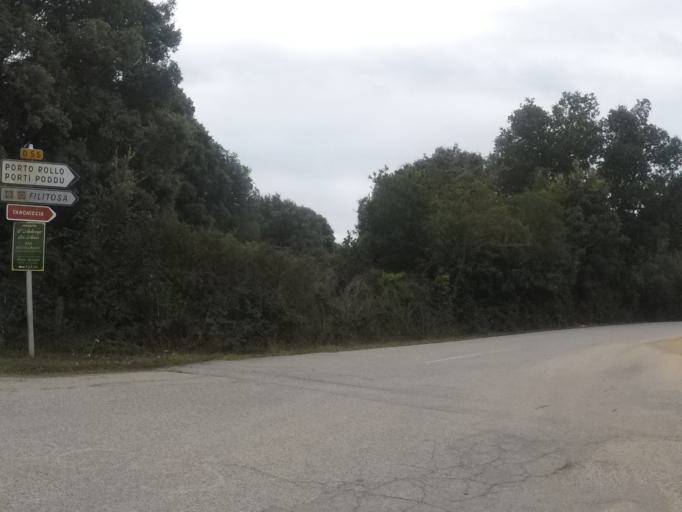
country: FR
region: Corsica
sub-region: Departement de la Corse-du-Sud
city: Pietrosella
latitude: 41.8103
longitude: 8.8483
